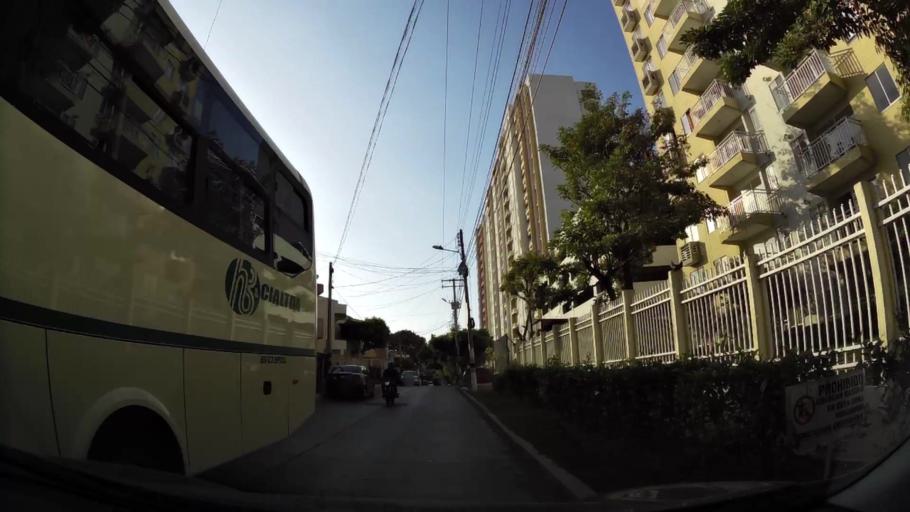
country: CO
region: Bolivar
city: Cartagena
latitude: 10.3877
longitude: -75.4794
